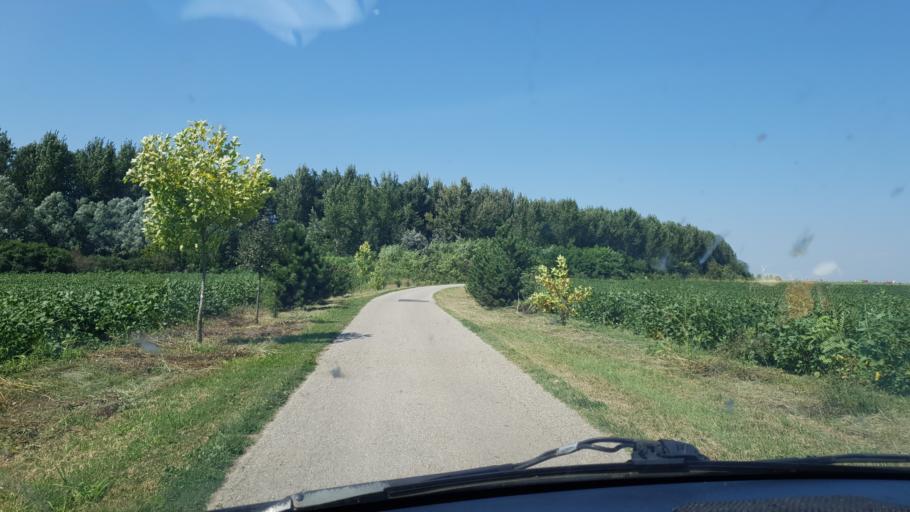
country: RS
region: Autonomna Pokrajina Vojvodina
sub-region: Juznobacki Okrug
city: Kovilj
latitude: 45.2009
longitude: 20.0634
